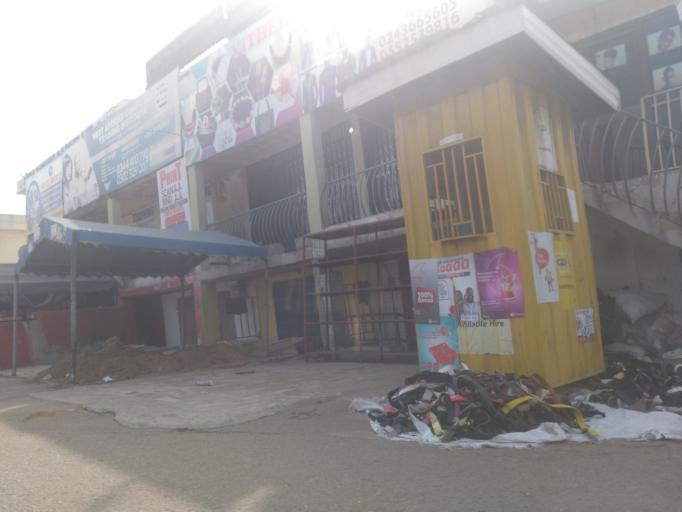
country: GH
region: Greater Accra
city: Gbawe
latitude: 5.5789
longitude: -0.2673
